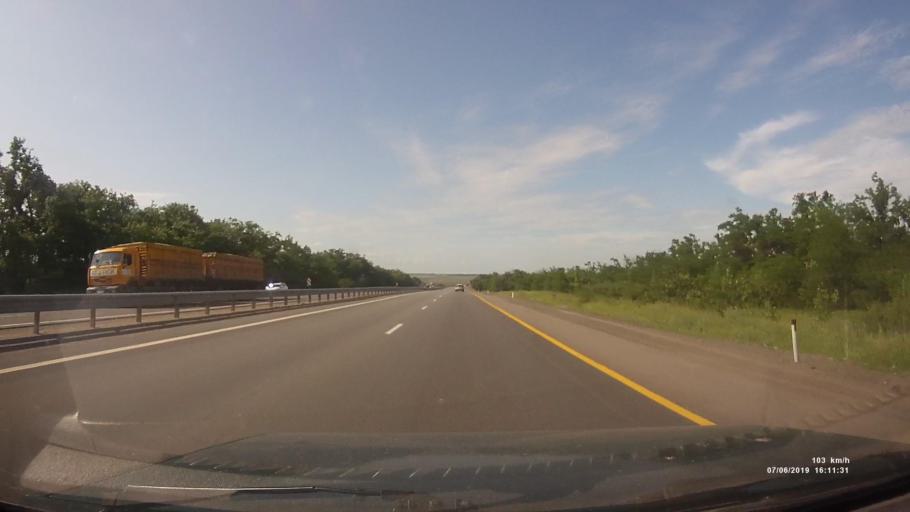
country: RU
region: Rostov
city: Likhoy
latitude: 48.1149
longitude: 40.2591
